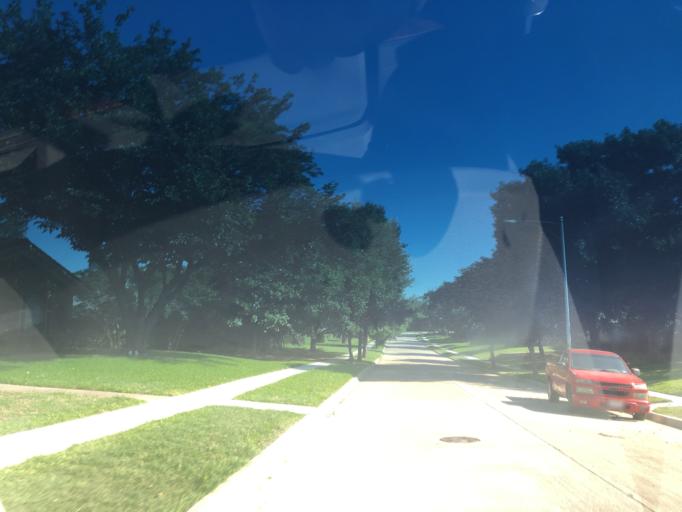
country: US
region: Texas
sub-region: Dallas County
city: Grand Prairie
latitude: 32.7176
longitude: -97.0191
